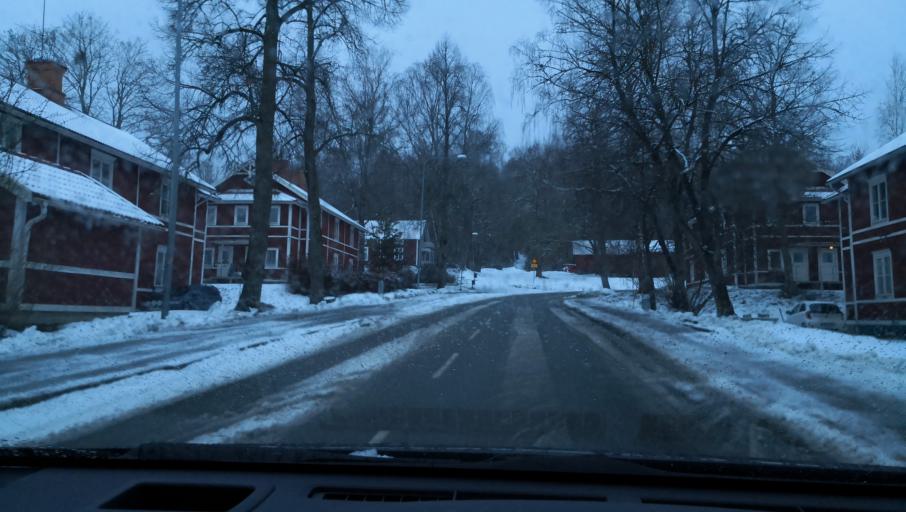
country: SE
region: Vaestmanland
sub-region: Kopings Kommun
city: Kolsva
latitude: 59.5959
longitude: 15.8310
